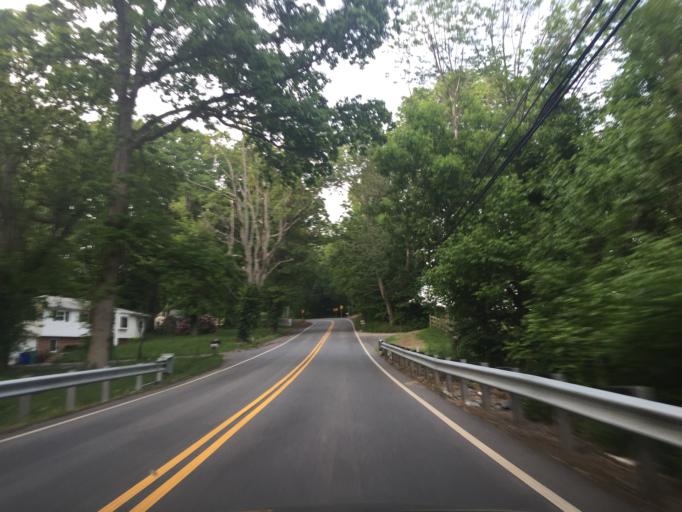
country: US
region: Maryland
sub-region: Frederick County
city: Brunswick
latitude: 39.3384
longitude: -77.6094
